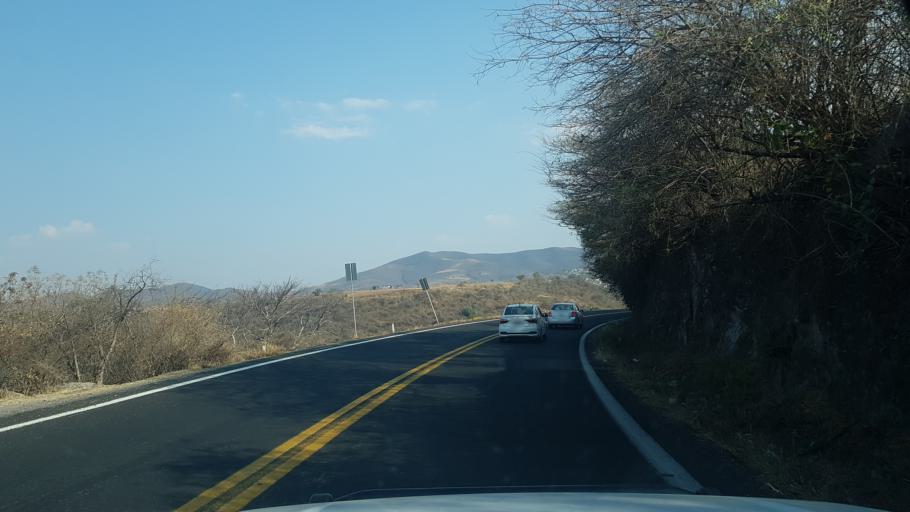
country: MX
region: Puebla
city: Calmeca
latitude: 18.6525
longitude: -98.6449
